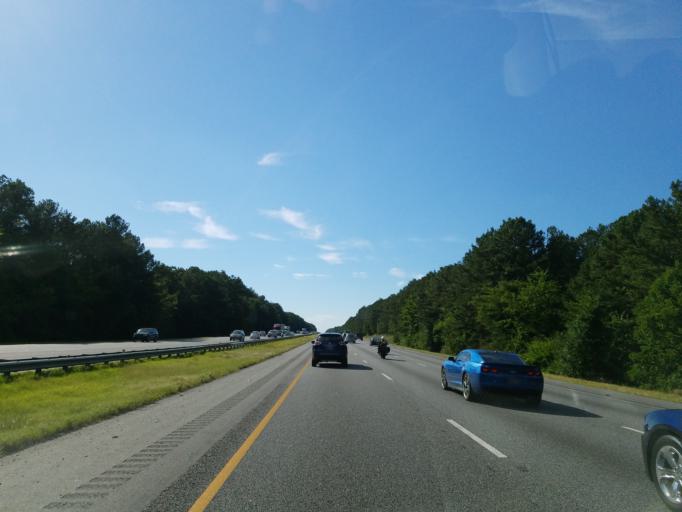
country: US
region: Georgia
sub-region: Bartow County
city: Rydal
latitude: 34.3001
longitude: -84.8278
